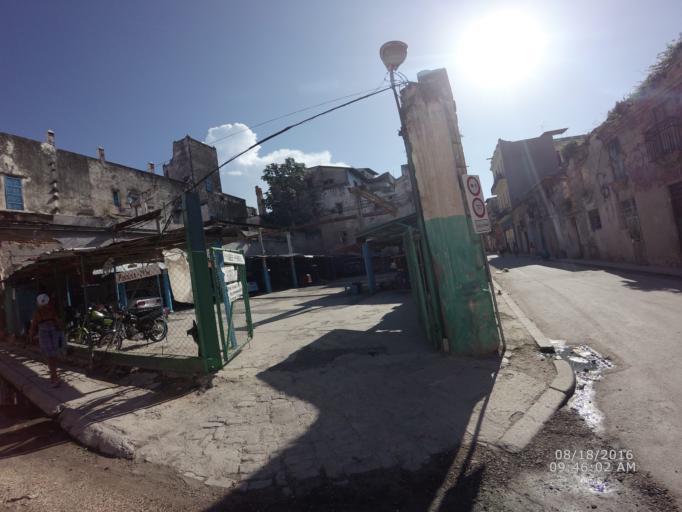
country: CU
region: La Habana
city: La Habana Vieja
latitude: 23.1344
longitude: -82.3499
